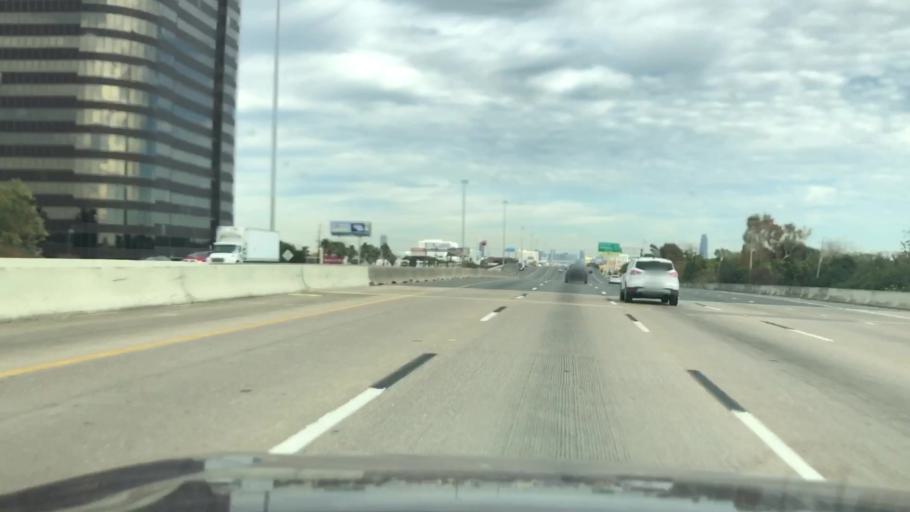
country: US
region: Texas
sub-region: Harris County
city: Bellaire
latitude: 29.7004
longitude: -95.5174
